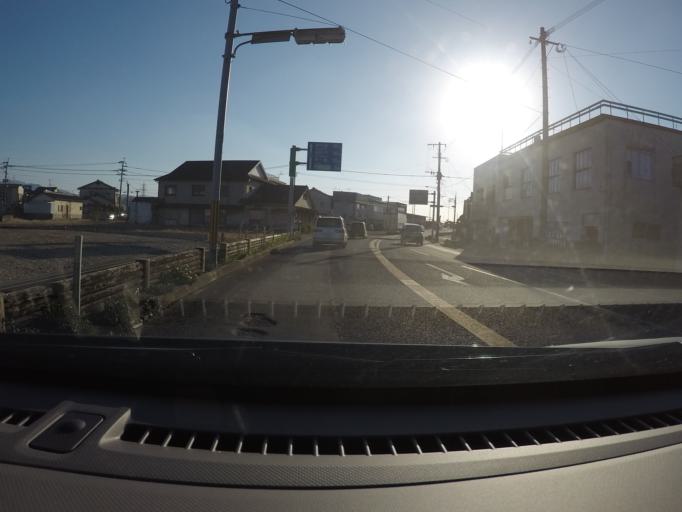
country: JP
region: Kagoshima
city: Izumi
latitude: 32.1168
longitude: 130.3398
